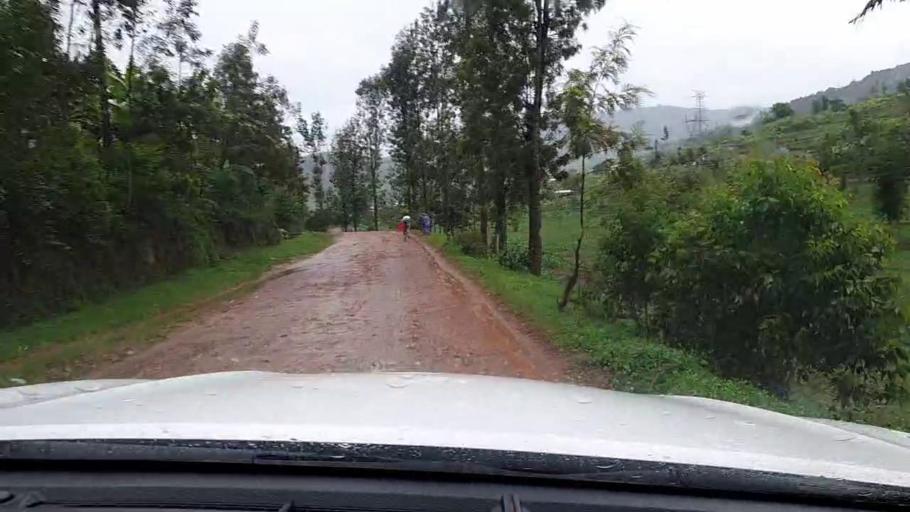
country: RW
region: Northern Province
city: Byumba
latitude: -1.7271
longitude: 29.9348
